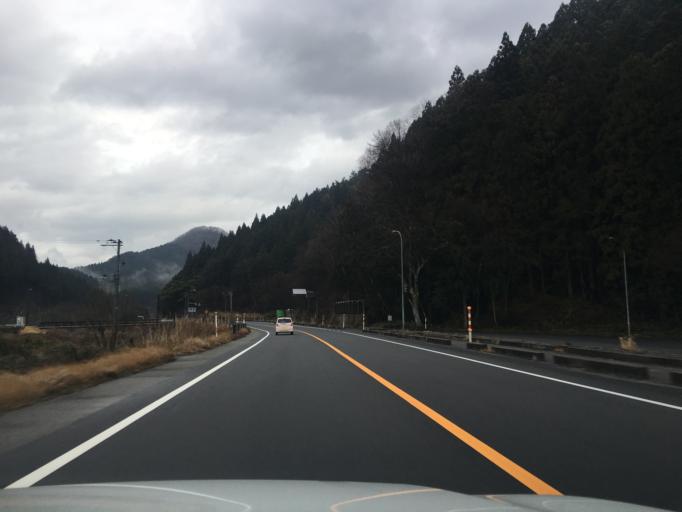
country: JP
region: Niigata
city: Murakami
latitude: 38.4689
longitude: 139.5568
